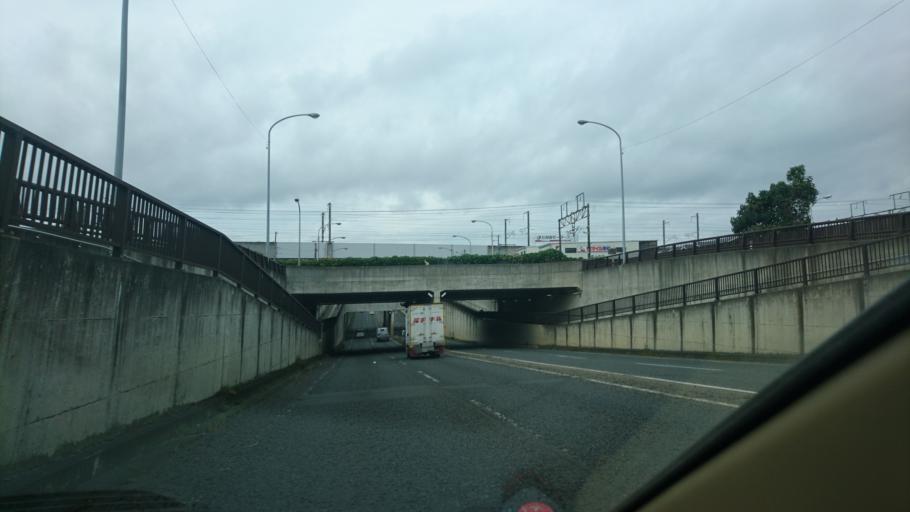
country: JP
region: Iwate
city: Morioka-shi
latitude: 39.6845
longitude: 141.1497
